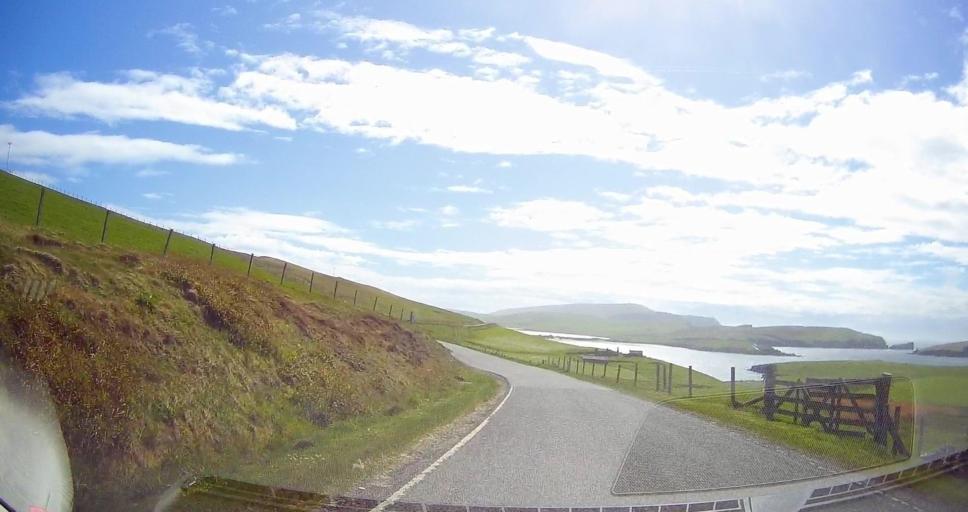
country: GB
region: Scotland
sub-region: Shetland Islands
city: Sandwick
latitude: 59.9582
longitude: -1.3259
